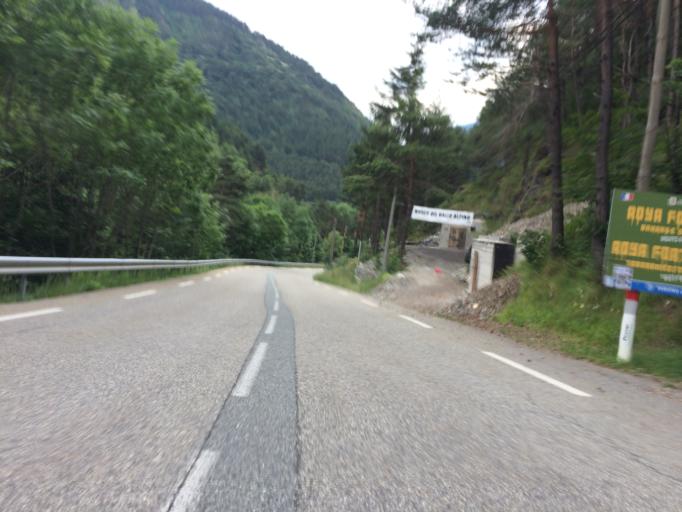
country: FR
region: Provence-Alpes-Cote d'Azur
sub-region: Departement des Alpes-Maritimes
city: Tende
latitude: 44.1222
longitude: 7.5673
